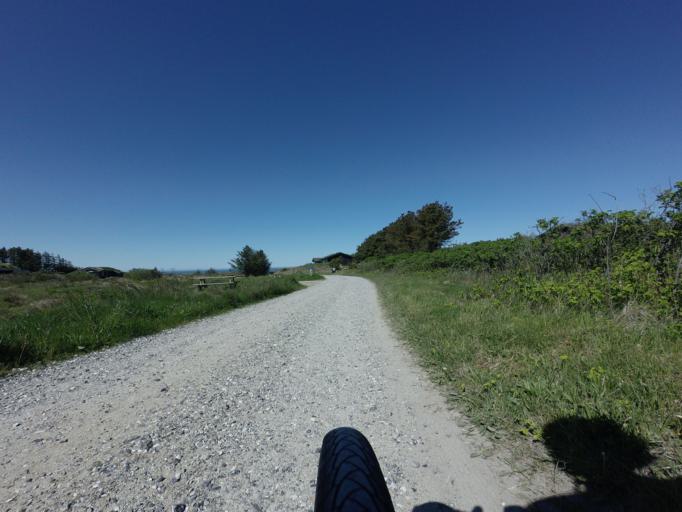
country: DK
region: North Denmark
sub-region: Jammerbugt Kommune
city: Pandrup
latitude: 57.3000
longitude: 9.6481
